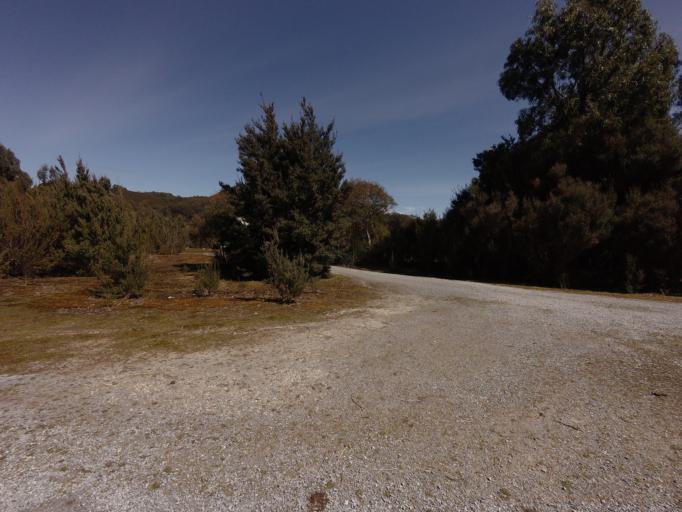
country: AU
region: Tasmania
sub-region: Huon Valley
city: Geeveston
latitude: -43.0301
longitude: 146.3501
